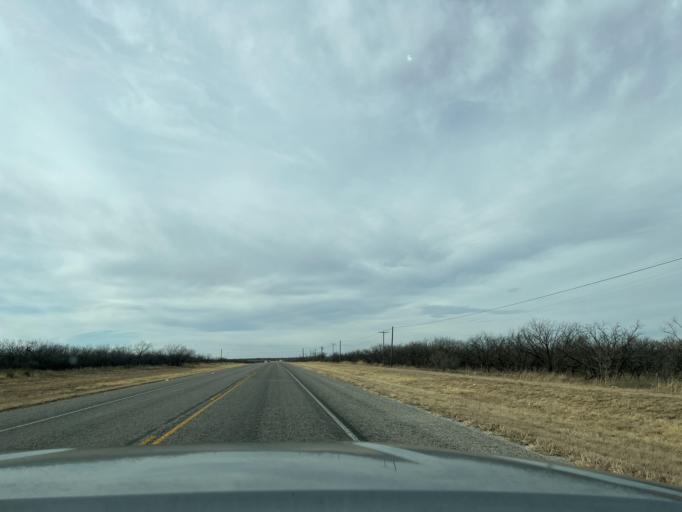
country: US
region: Texas
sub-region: Shackelford County
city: Albany
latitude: 32.7587
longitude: -99.5662
